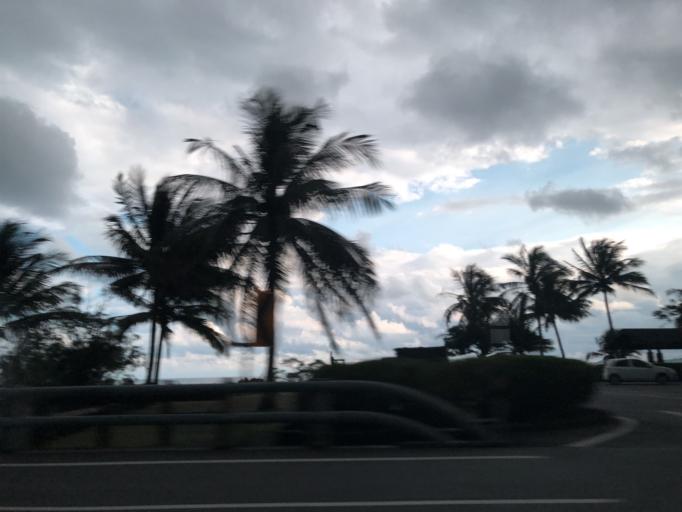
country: TW
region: Taiwan
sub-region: Taitung
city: Taitung
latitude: 22.8617
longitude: 121.2041
